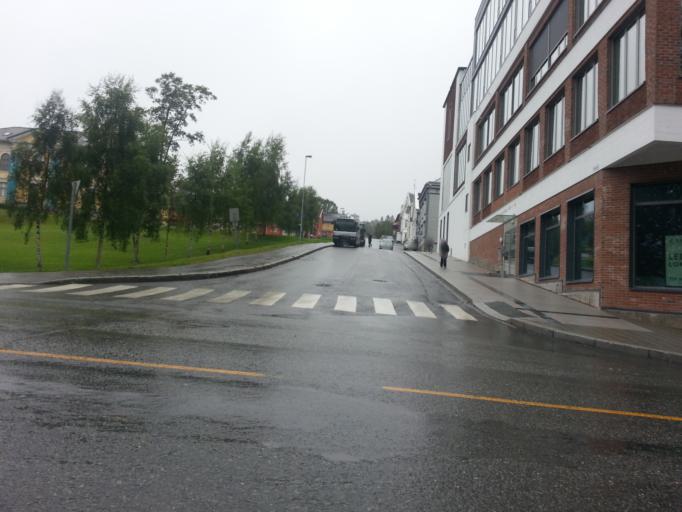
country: NO
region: Troms
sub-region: Tromso
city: Tromso
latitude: 69.6454
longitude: 18.9498
